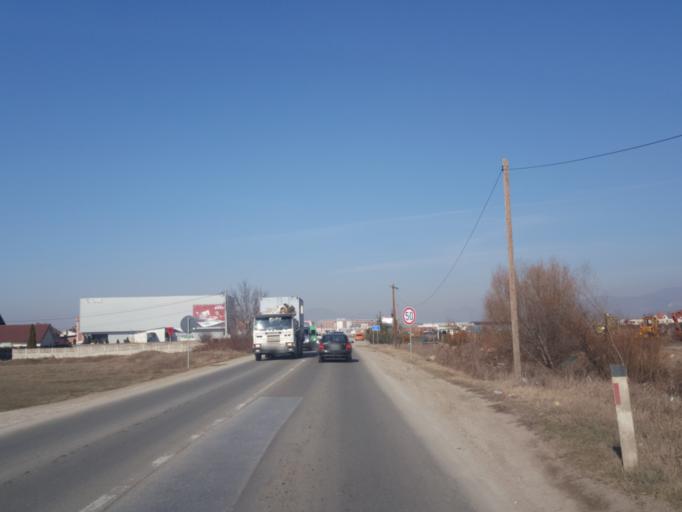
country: XK
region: Mitrovica
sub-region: Vushtrri
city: Vushtrri
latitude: 42.8097
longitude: 20.9874
